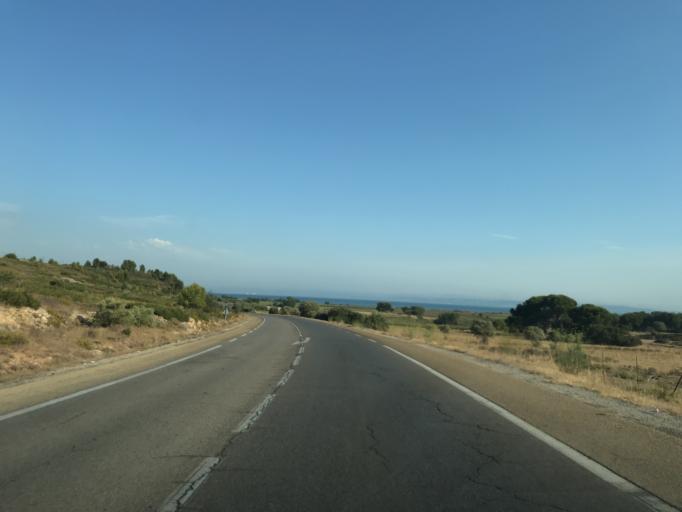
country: FR
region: Provence-Alpes-Cote d'Azur
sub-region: Departement des Bouches-du-Rhone
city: Saint-Chamas
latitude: 43.5343
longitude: 5.0478
